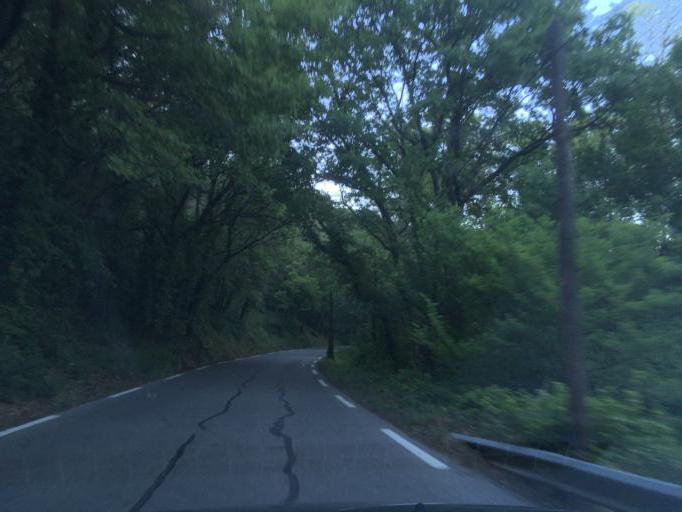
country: FR
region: Provence-Alpes-Cote d'Azur
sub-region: Departement du Var
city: Salernes
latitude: 43.5343
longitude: 6.2483
